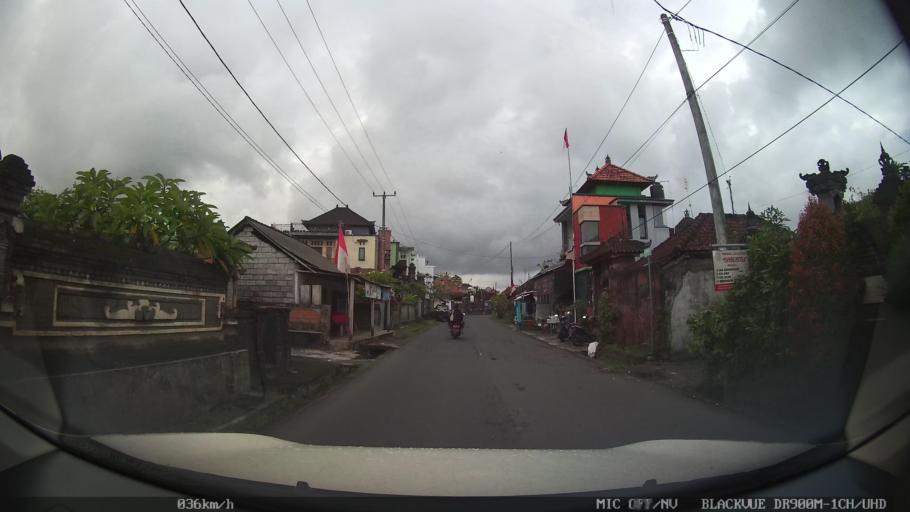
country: ID
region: Bali
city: Banjar Cemenggon
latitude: -8.5545
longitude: 115.1910
